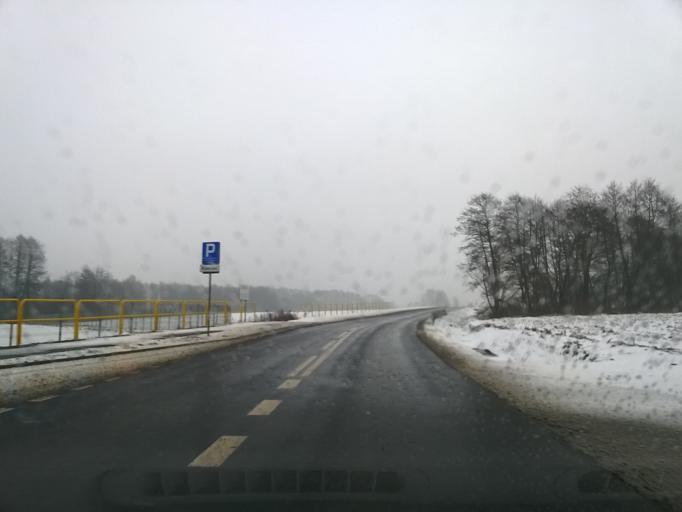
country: PL
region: Kujawsko-Pomorskie
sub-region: Powiat swiecki
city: Swiecie
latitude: 53.4267
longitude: 18.4092
